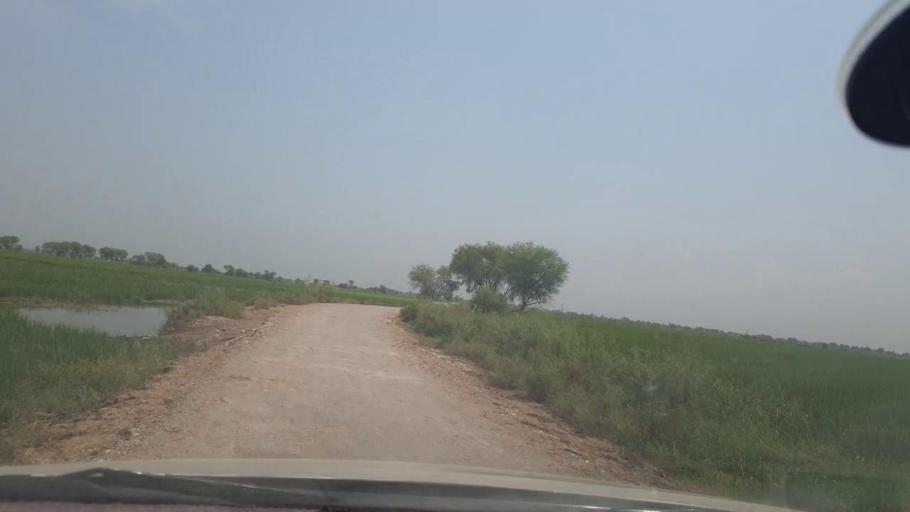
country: PK
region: Sindh
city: Jacobabad
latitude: 28.1715
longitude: 68.3898
